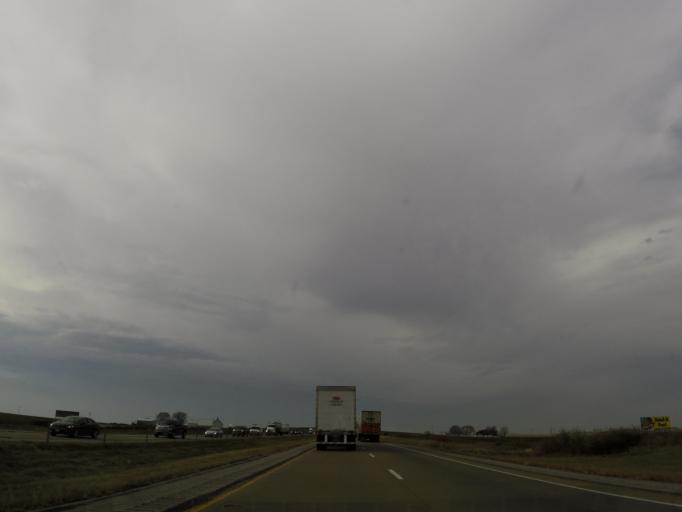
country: US
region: Iowa
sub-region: Scott County
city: Walcott
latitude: 41.6073
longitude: -90.7373
